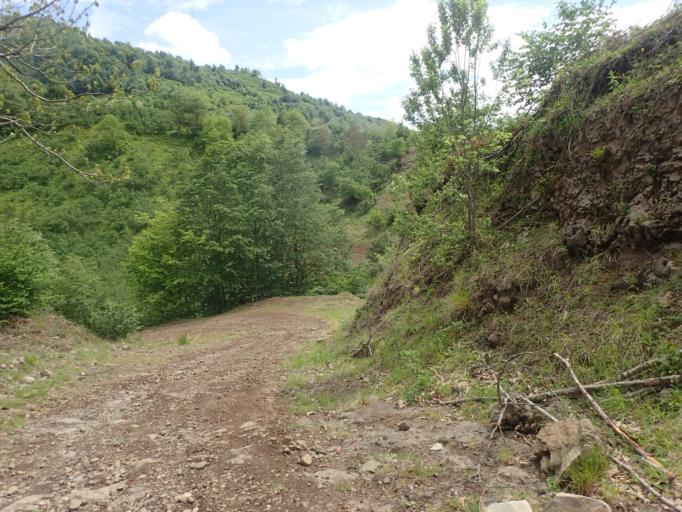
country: TR
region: Samsun
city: Salipazari
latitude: 40.9245
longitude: 36.8992
